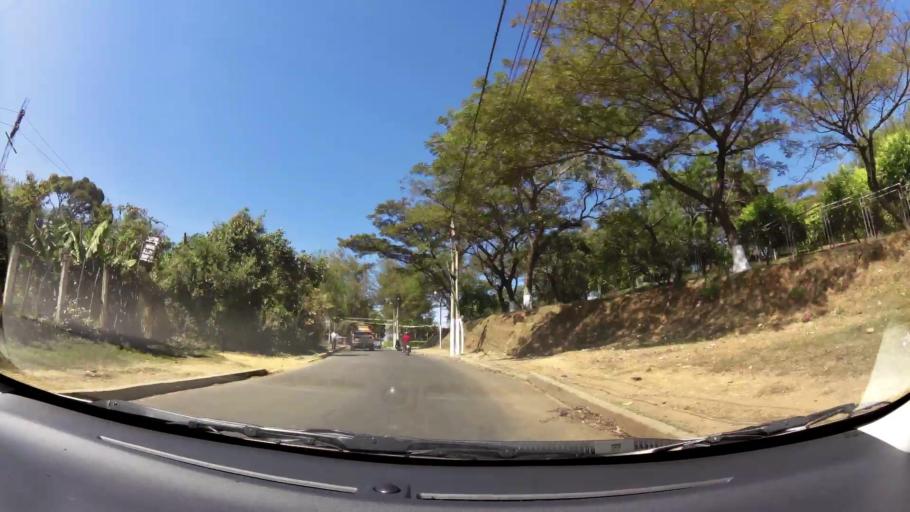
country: SV
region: Ahuachapan
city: Ahuachapan
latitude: 13.9359
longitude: -89.8567
